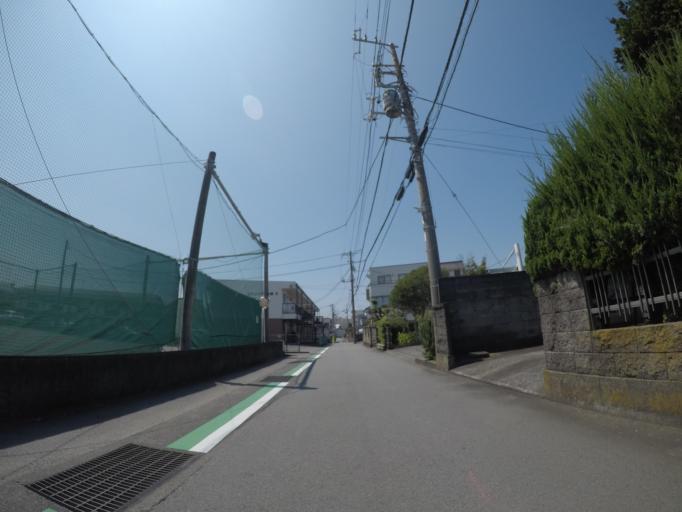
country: JP
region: Shizuoka
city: Numazu
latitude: 35.1141
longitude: 138.8757
